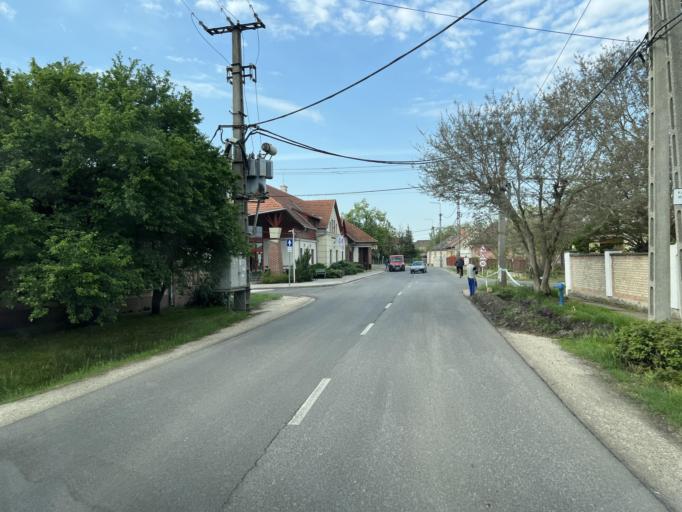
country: HU
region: Pest
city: Abony
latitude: 47.1915
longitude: 20.0098
